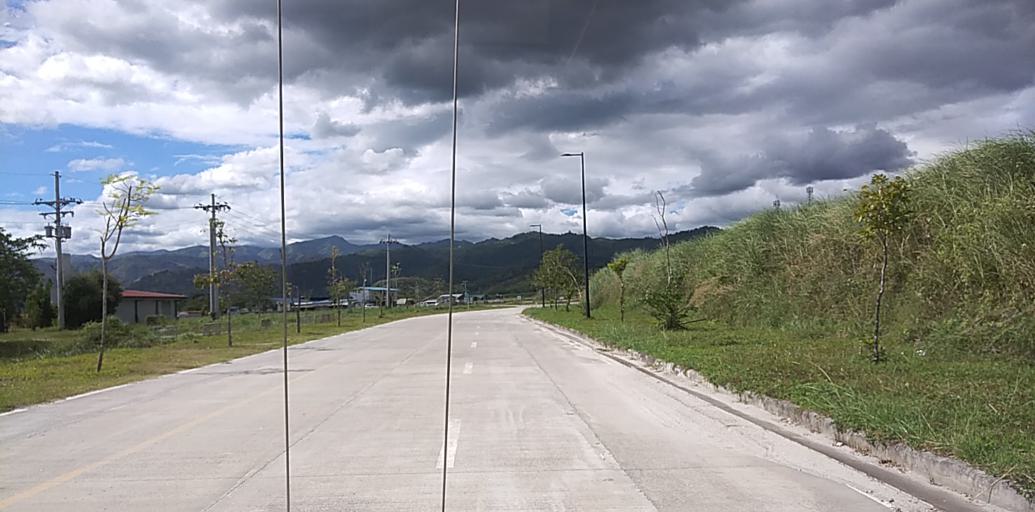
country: PH
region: Central Luzon
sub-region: Province of Pampanga
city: Dolores
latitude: 15.1141
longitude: 120.5099
